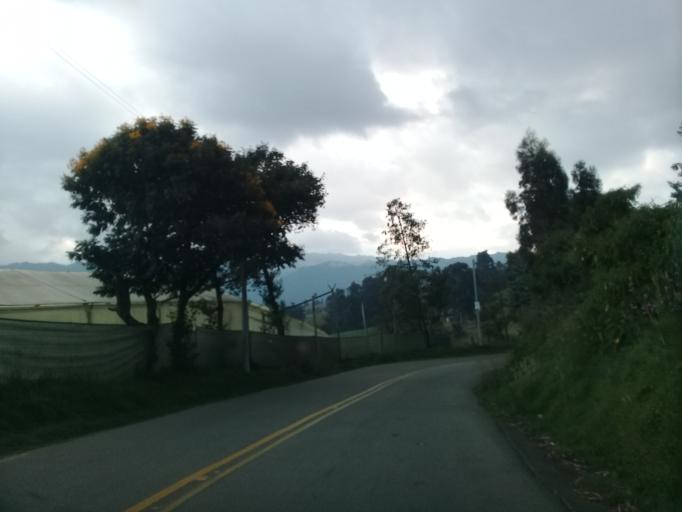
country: CO
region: Cundinamarca
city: Zipaquira
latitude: 5.0379
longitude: -74.0452
